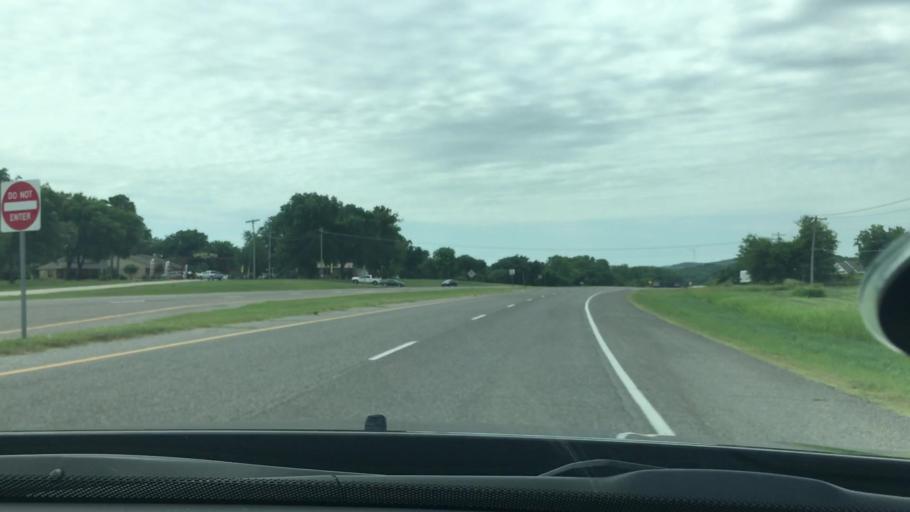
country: US
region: Oklahoma
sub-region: Murray County
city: Davis
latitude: 34.4628
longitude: -97.1308
